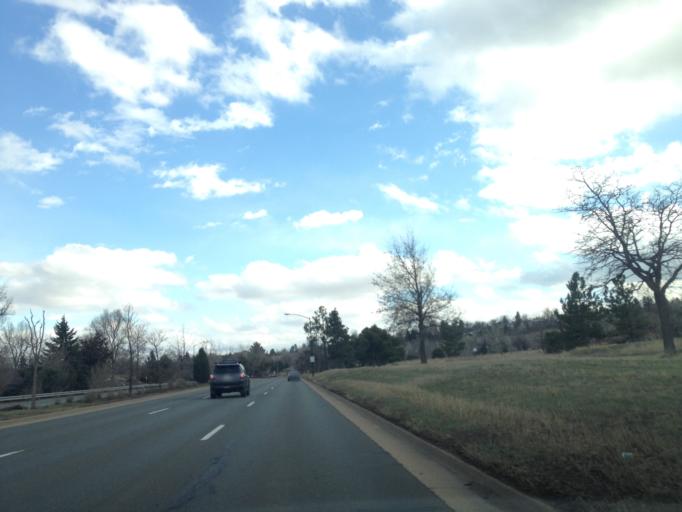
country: US
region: Colorado
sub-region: Boulder County
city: Boulder
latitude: 39.9924
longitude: -105.2584
